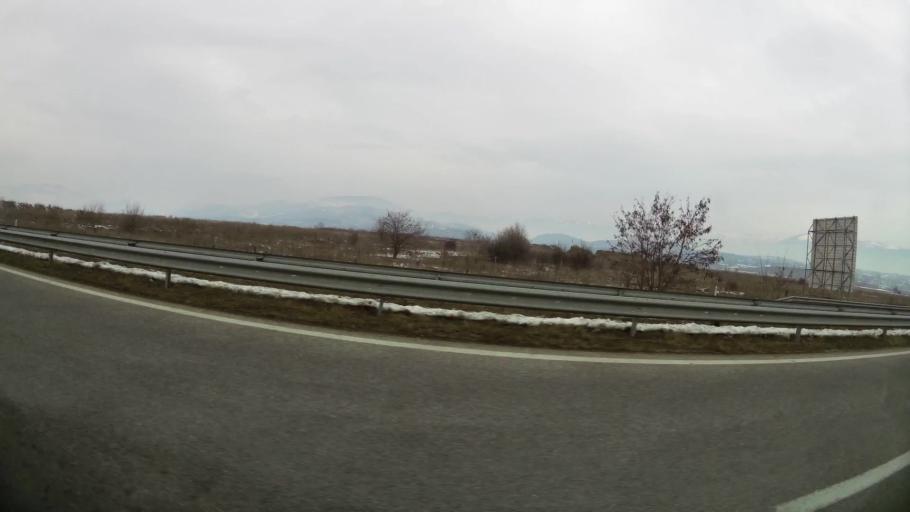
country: MK
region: Suto Orizari
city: Suto Orizare
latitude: 42.0530
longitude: 21.3935
